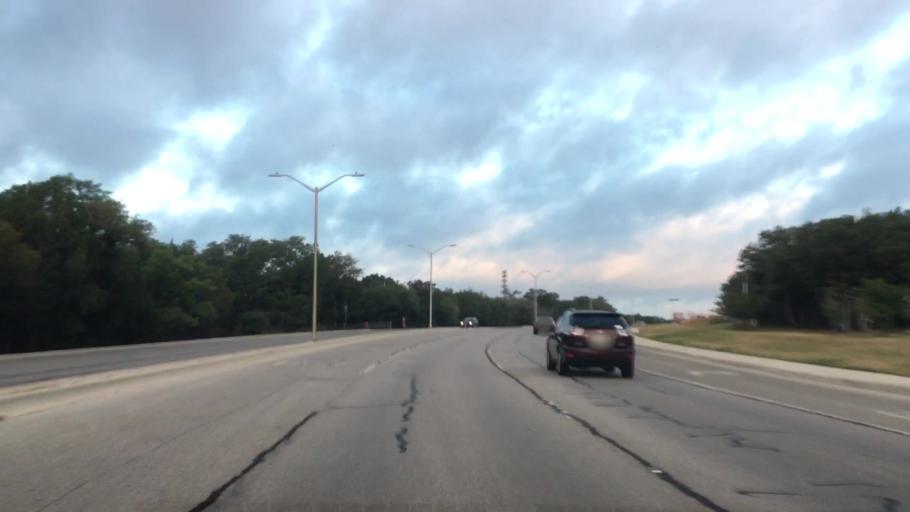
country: US
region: Texas
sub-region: Williamson County
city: Brushy Creek
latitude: 30.5071
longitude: -97.7789
